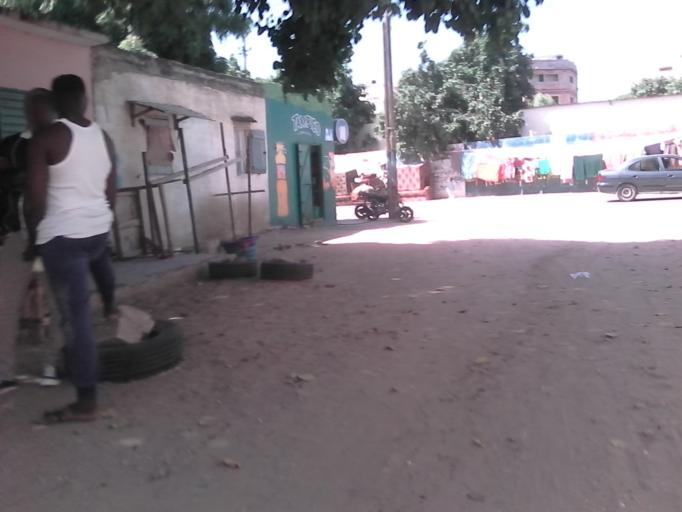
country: SN
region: Dakar
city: Grand Dakar
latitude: 14.7056
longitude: -17.4533
